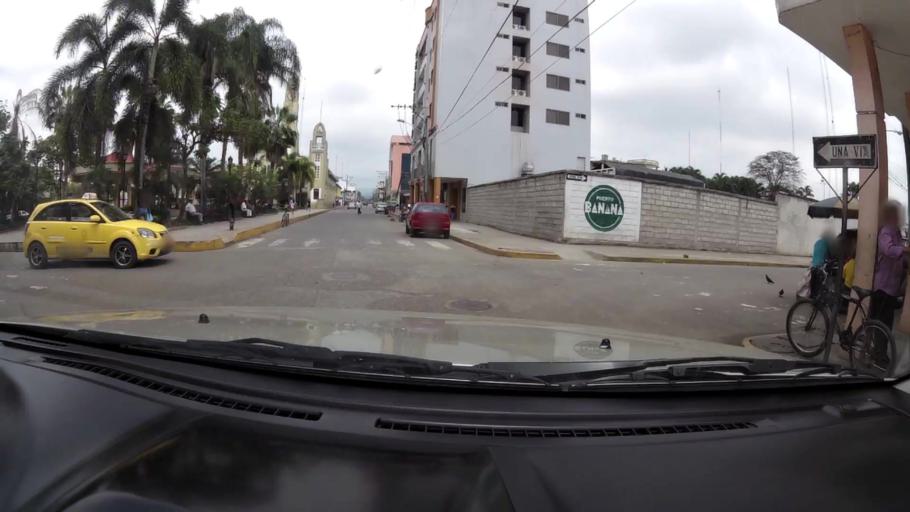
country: EC
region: El Oro
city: Pasaje
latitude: -3.2456
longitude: -79.8322
